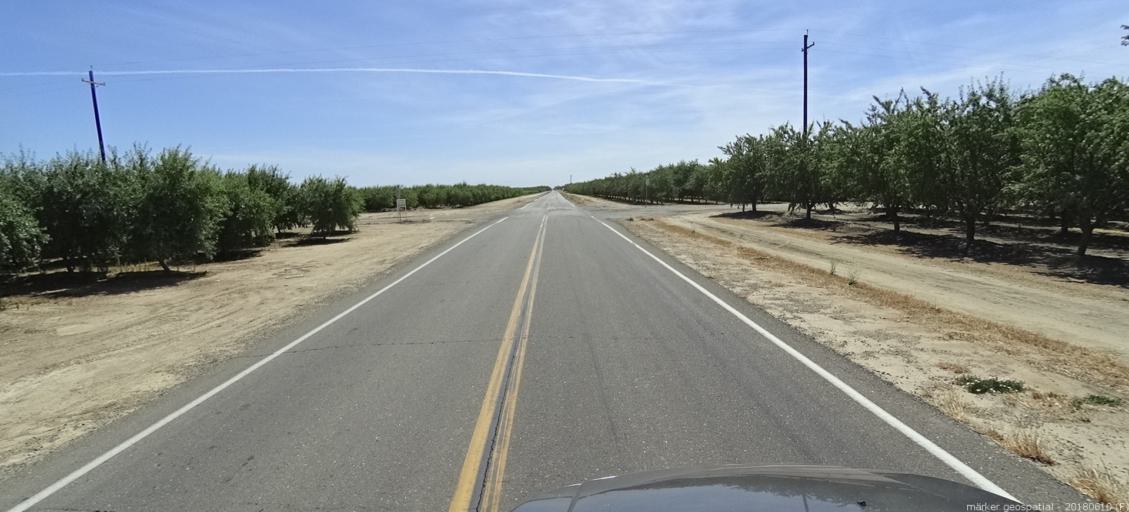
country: US
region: California
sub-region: Madera County
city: Fairmead
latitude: 37.0183
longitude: -120.2751
